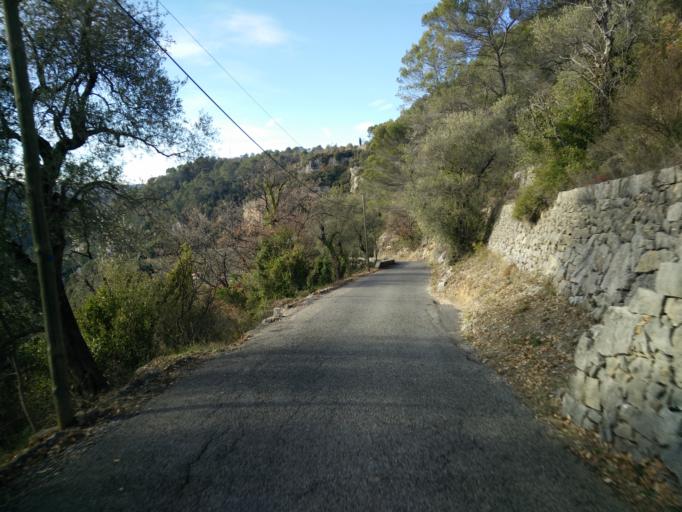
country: FR
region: Provence-Alpes-Cote d'Azur
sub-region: Departement des Alpes-Maritimes
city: Saint-Cezaire-sur-Siagne
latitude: 43.6621
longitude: 6.7781
